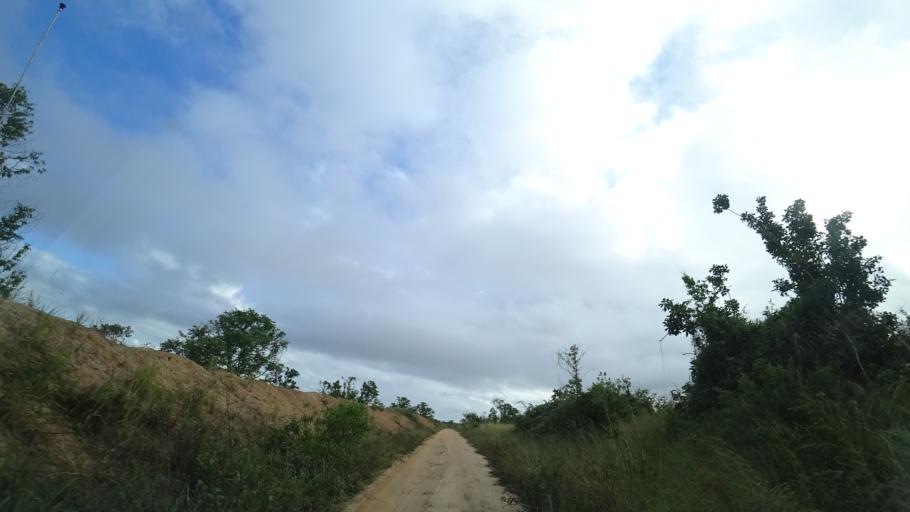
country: MZ
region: Sofala
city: Beira
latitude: -19.6202
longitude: 35.0605
